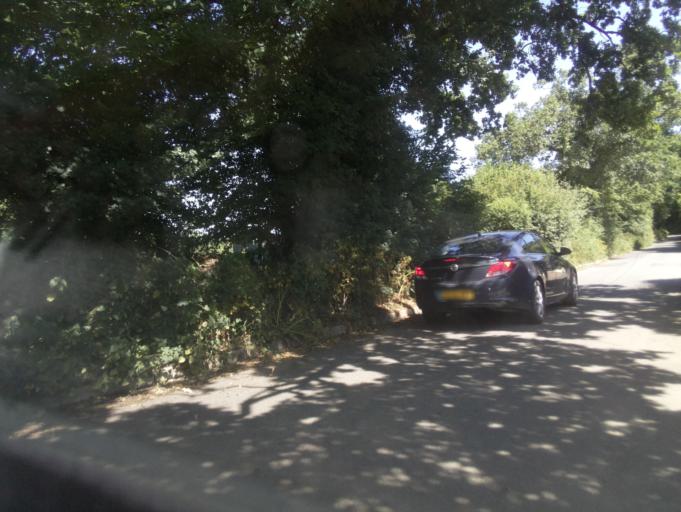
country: GB
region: England
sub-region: Devon
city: Ipplepen
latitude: 50.5008
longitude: -3.6271
